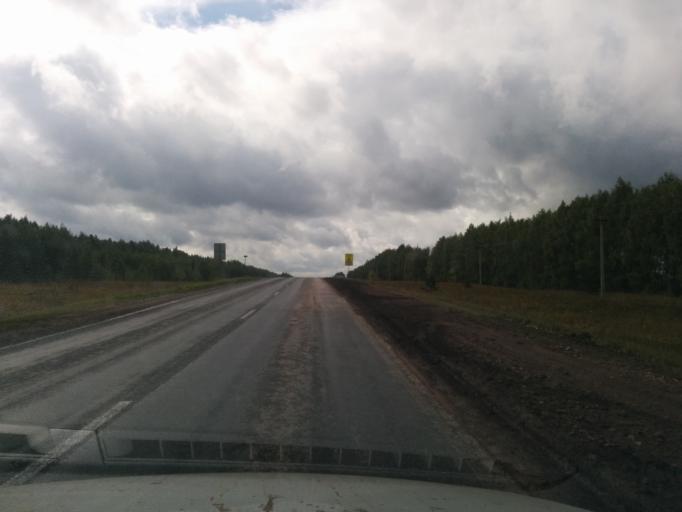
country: RU
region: Tatarstan
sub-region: Bugul'minskiy Rayon
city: Bugul'ma
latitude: 54.2609
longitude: 52.9132
